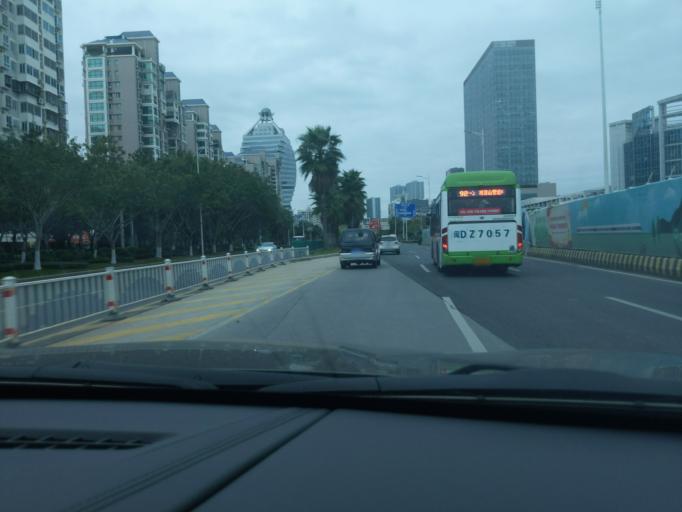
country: CN
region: Fujian
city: Liuwudian
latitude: 24.4838
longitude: 118.1795
